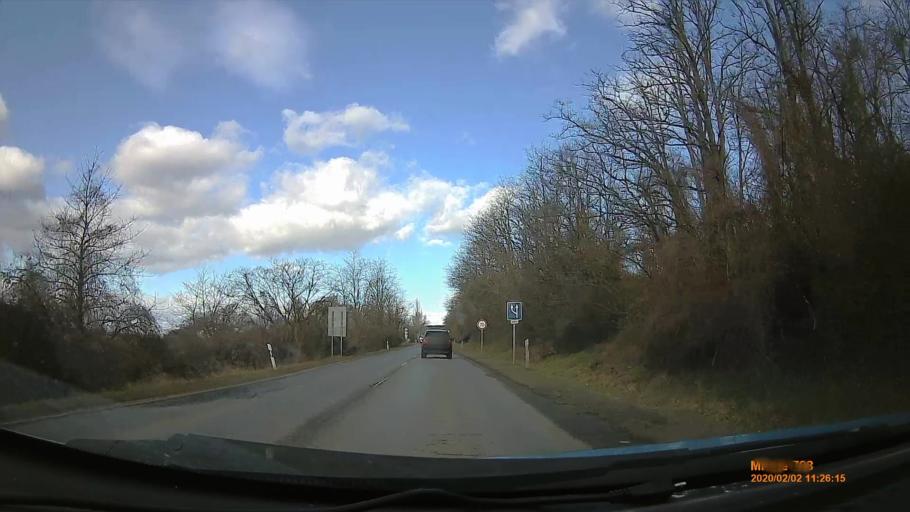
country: HU
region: Gyor-Moson-Sopron
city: Sopron
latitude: 47.7053
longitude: 16.5769
